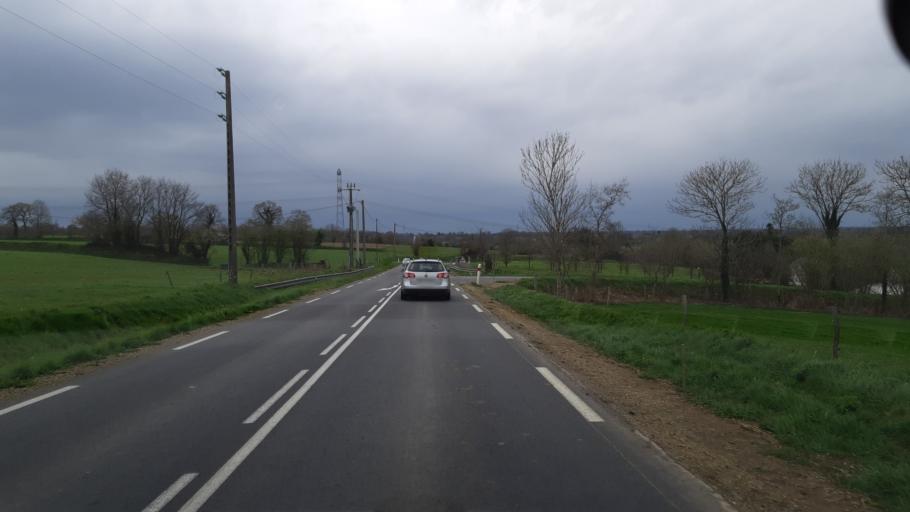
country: FR
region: Lower Normandy
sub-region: Departement de la Manche
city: Percy
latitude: 48.9591
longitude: -1.1827
